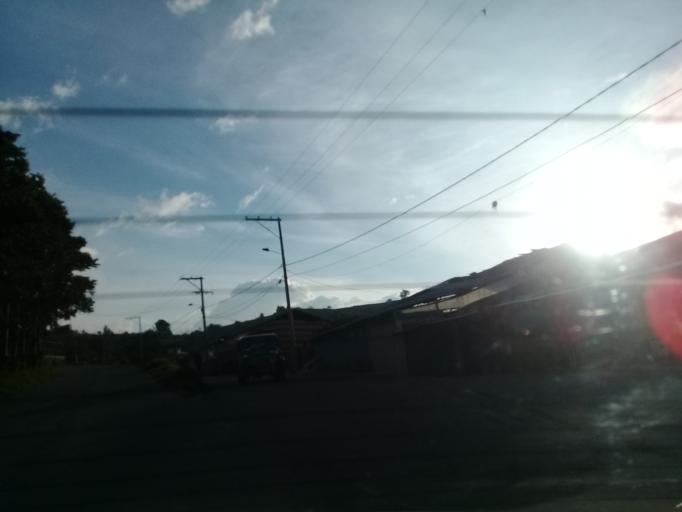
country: CO
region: Cundinamarca
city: Sibate
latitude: 4.4635
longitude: -74.2654
